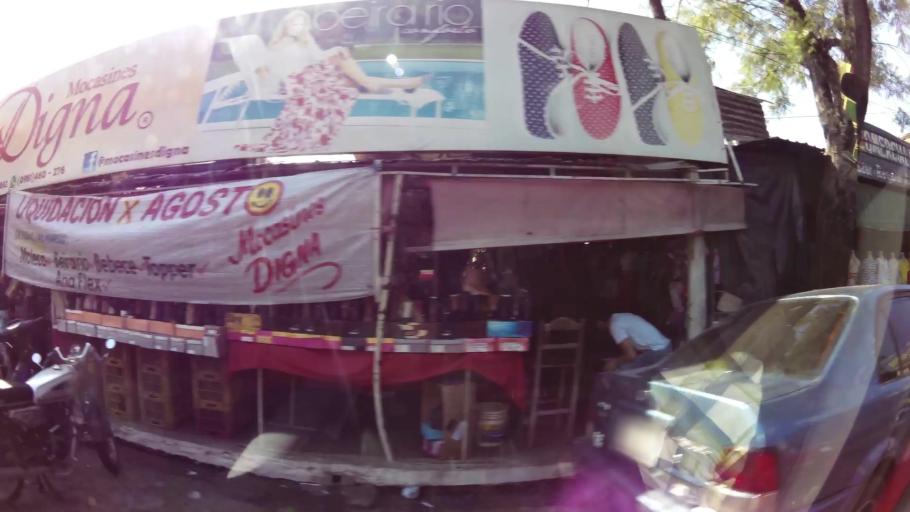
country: PY
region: Central
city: San Lorenzo
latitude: -25.3464
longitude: -57.5104
